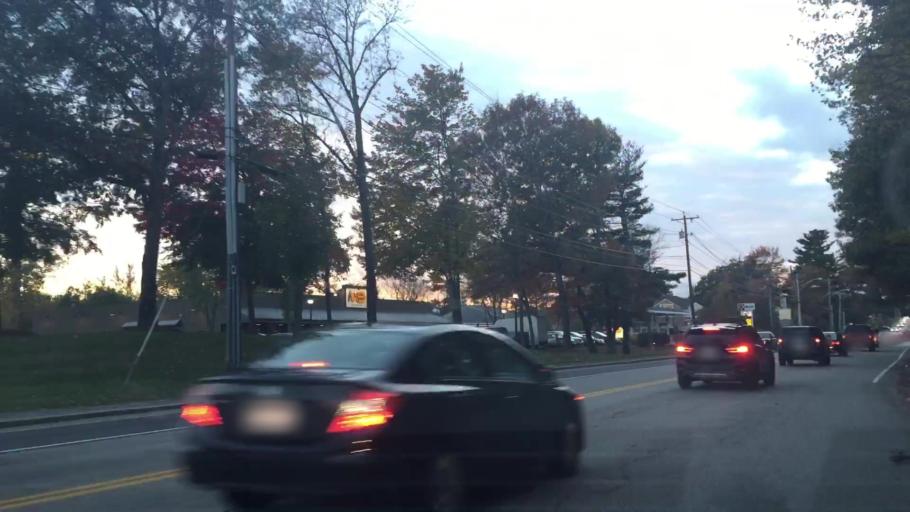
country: US
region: Massachusetts
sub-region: Middlesex County
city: Tewksbury
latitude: 42.6429
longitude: -71.2341
